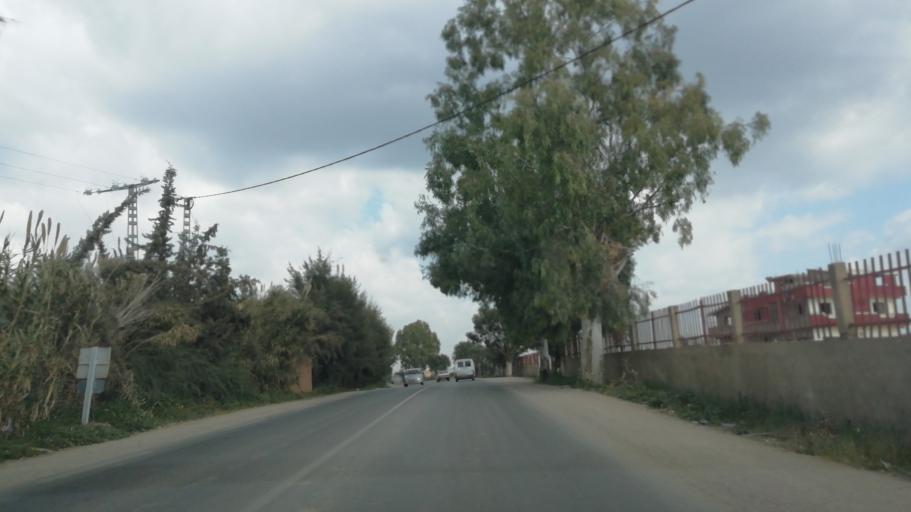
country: DZ
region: Mascara
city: Mascara
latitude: 35.6281
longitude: 0.1269
